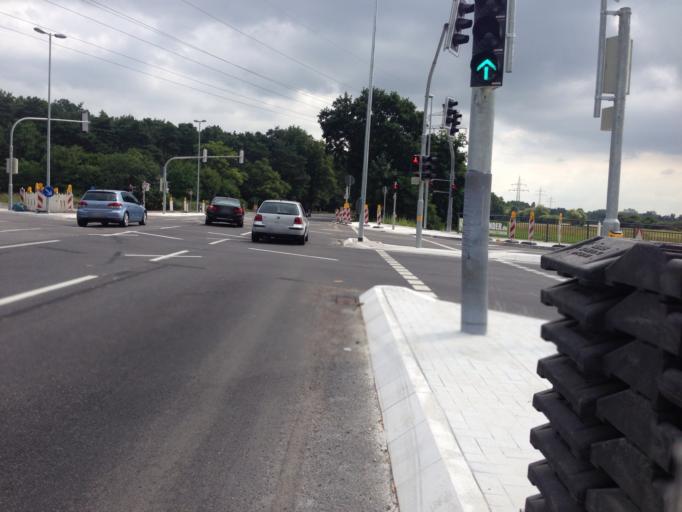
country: DE
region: Hesse
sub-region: Regierungsbezirk Darmstadt
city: Hanau am Main
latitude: 50.1505
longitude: 8.9086
